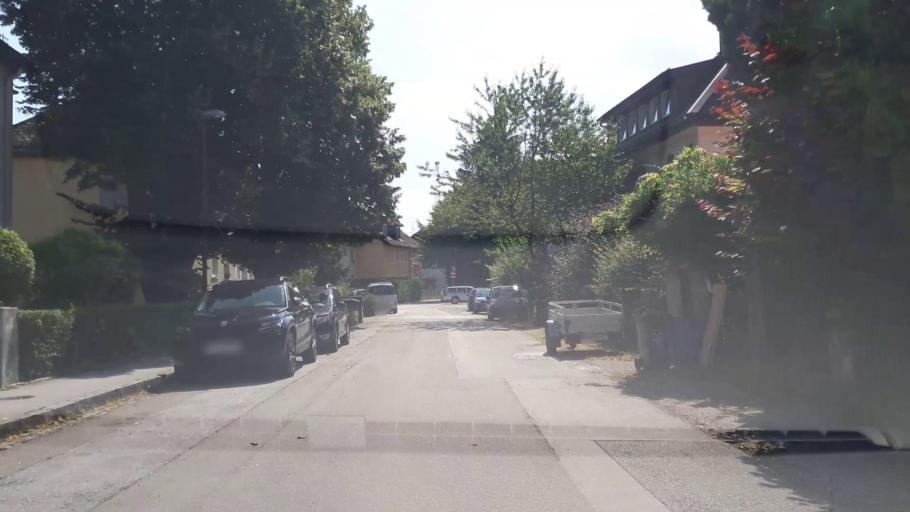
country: AT
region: Salzburg
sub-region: Salzburg Stadt
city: Salzburg
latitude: 47.8029
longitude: 13.0142
